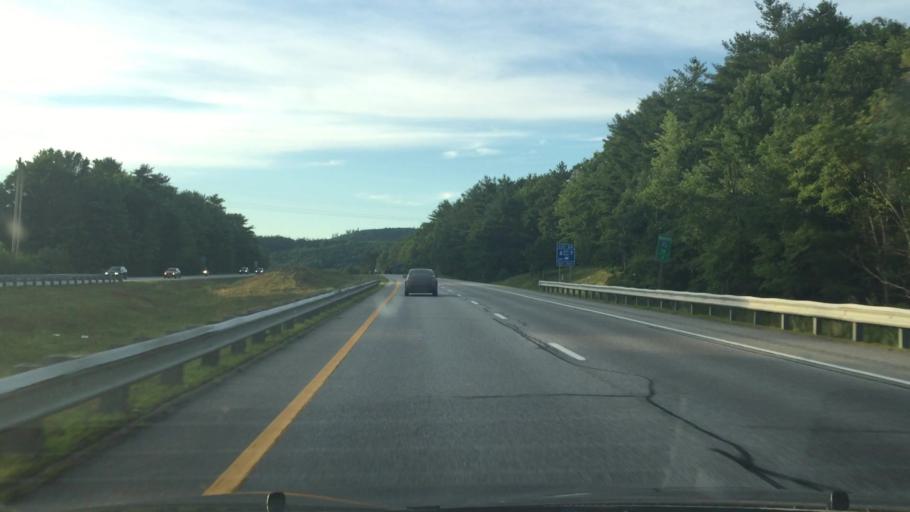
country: US
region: New Hampshire
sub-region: Grafton County
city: Ashland
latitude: 43.6879
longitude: -71.6422
